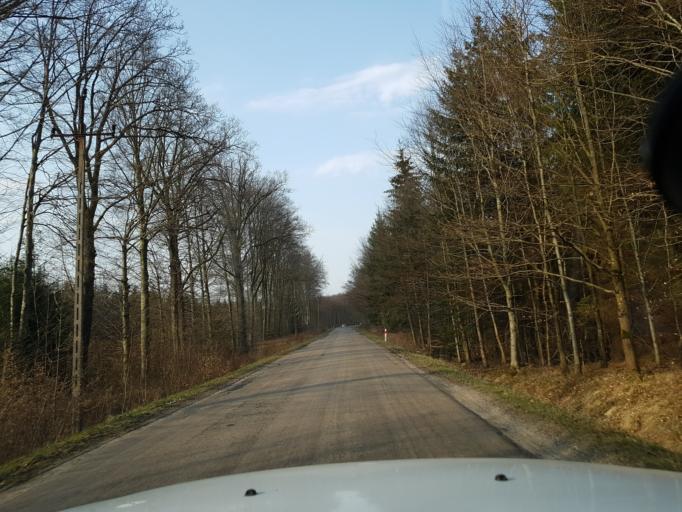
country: PL
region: West Pomeranian Voivodeship
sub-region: Powiat swidwinski
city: Polczyn-Zdroj
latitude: 53.7333
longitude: 16.0755
